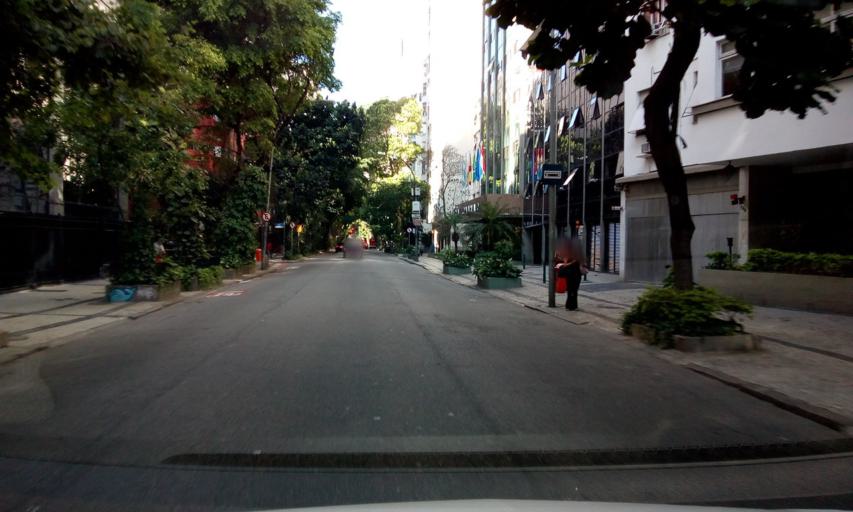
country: BR
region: Rio de Janeiro
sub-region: Rio De Janeiro
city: Rio de Janeiro
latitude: -22.9659
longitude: -43.1840
